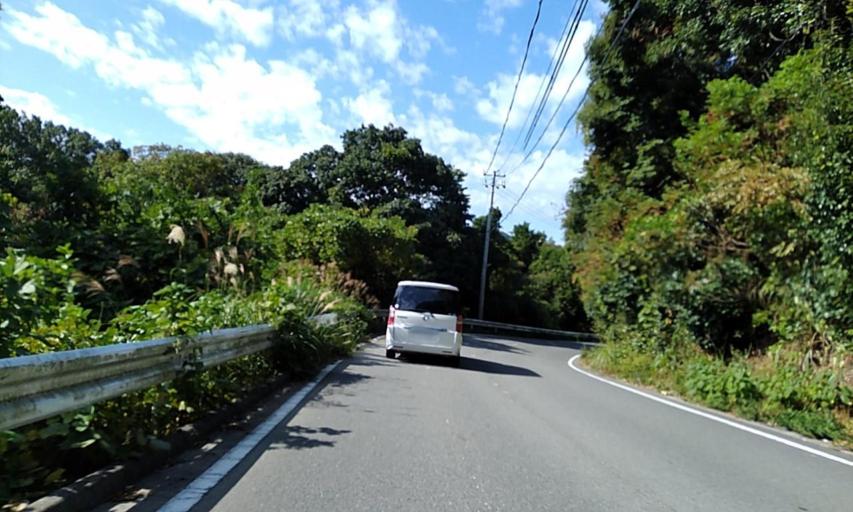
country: JP
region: Wakayama
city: Gobo
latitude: 33.9666
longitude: 135.1192
